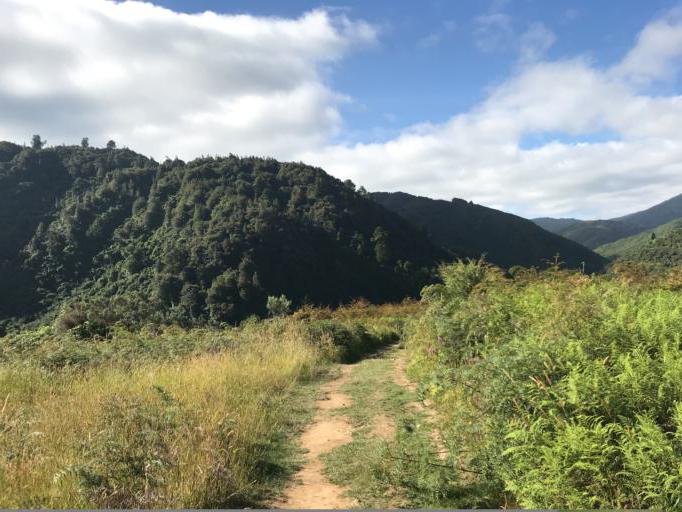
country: NZ
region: Wellington
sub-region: Kapiti Coast District
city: Otaki
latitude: -40.8724
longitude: 175.2345
